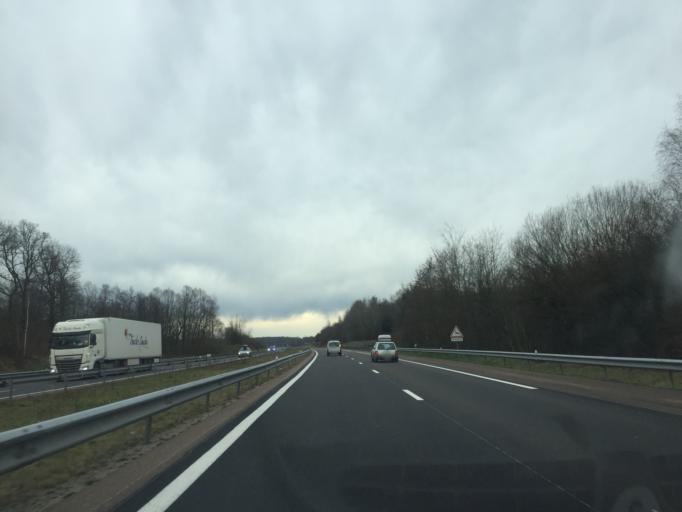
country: FR
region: Franche-Comte
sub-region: Departement du Jura
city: Bletterans
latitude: 46.8122
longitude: 5.5347
